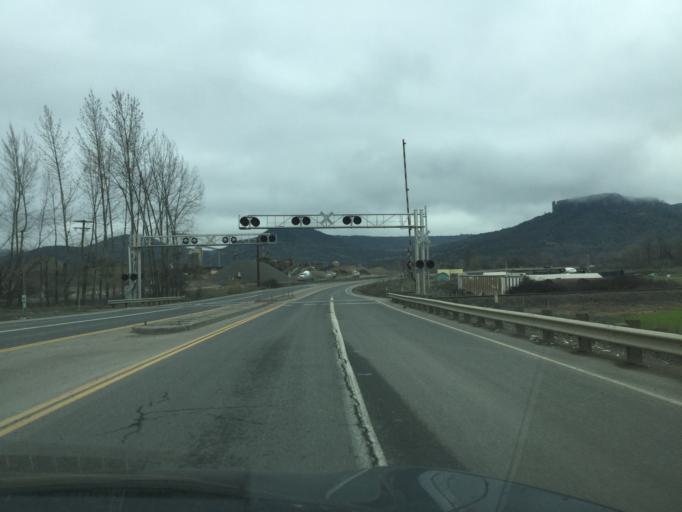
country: US
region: Oregon
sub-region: Jackson County
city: Central Point
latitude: 42.4213
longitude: -122.9579
